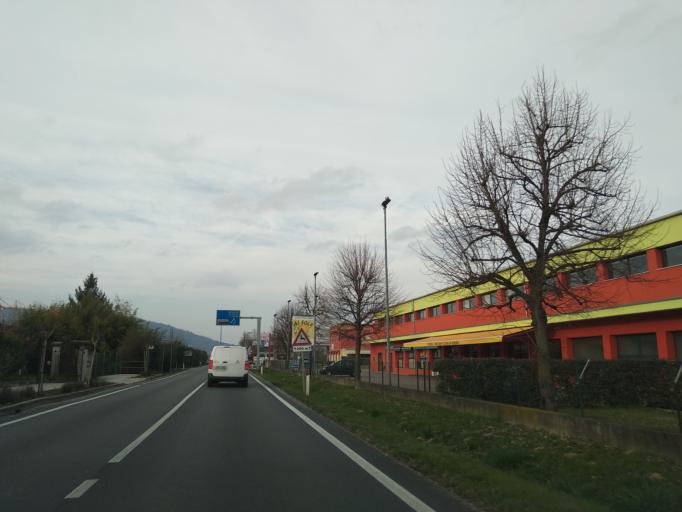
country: IT
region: Veneto
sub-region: Provincia di Vicenza
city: Ponte di Castegnero
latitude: 45.4405
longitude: 11.6008
